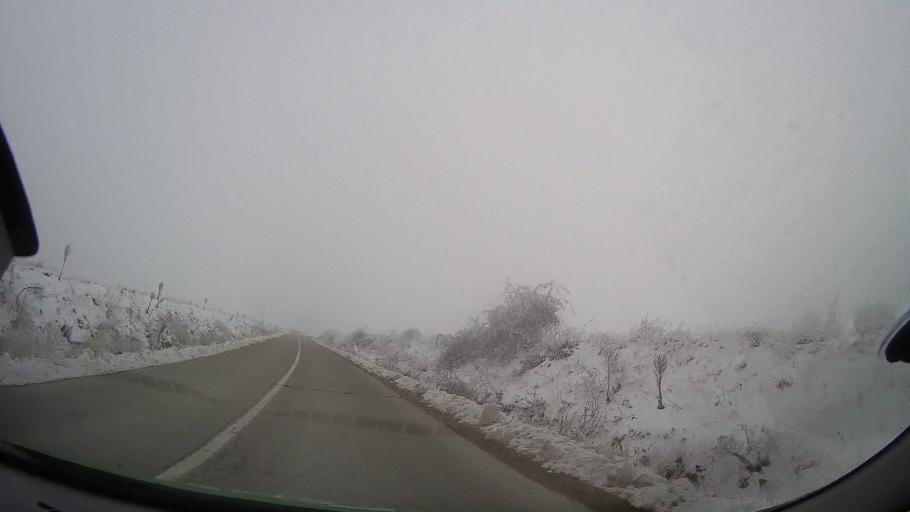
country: RO
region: Bacau
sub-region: Comuna Podu Turcului
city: Podu Turcului
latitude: 46.2088
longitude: 27.4202
